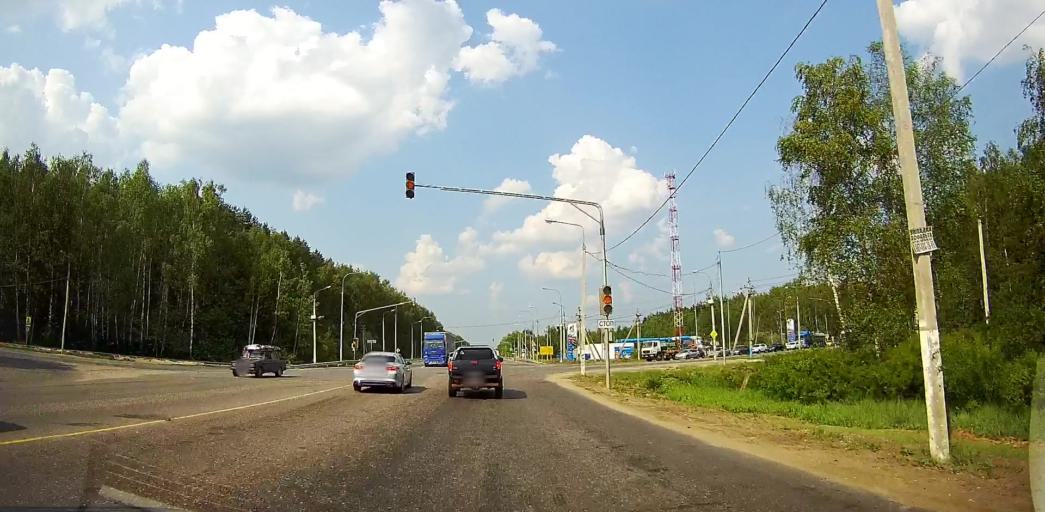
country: RU
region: Moskovskaya
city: Mikhnevo
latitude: 55.0769
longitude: 37.9520
